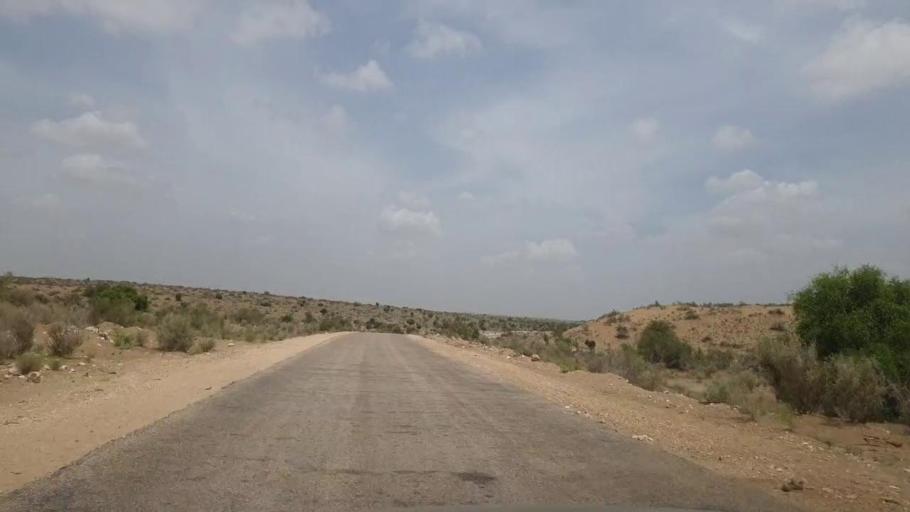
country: PK
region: Sindh
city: Kot Diji
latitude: 27.1700
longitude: 69.2080
